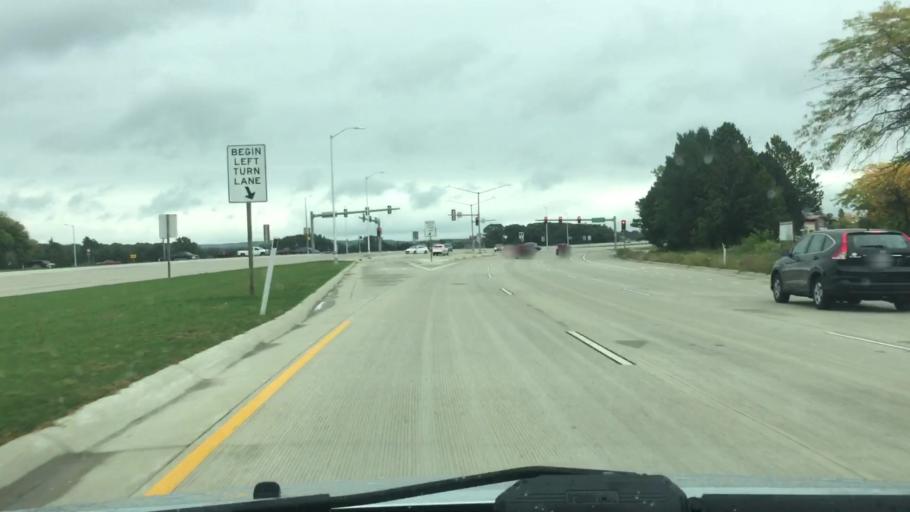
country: US
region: Wisconsin
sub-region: Waukesha County
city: Oconomowoc
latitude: 43.0884
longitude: -88.4722
